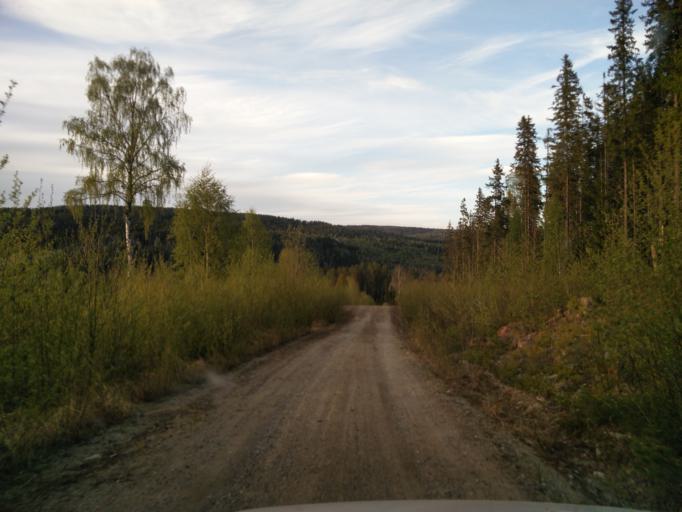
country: SE
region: Vaesternorrland
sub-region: Sundsvalls Kommun
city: Matfors
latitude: 62.4003
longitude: 16.8194
